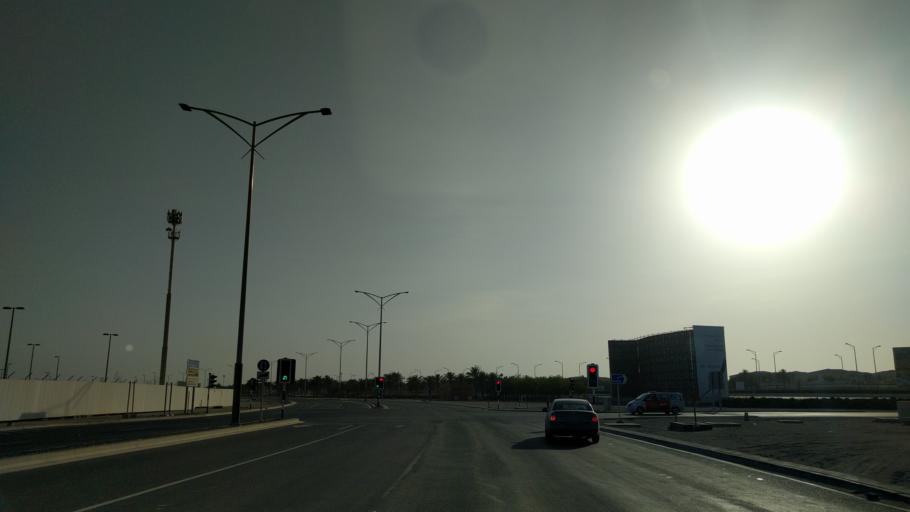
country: AE
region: Abu Dhabi
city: Abu Dhabi
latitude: 24.5461
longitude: 54.4527
